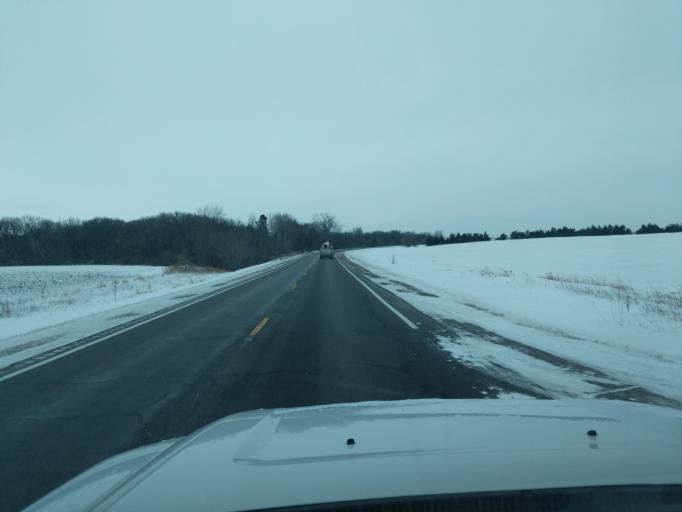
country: US
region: Minnesota
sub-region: Redwood County
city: Redwood Falls
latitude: 44.5707
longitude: -94.9946
